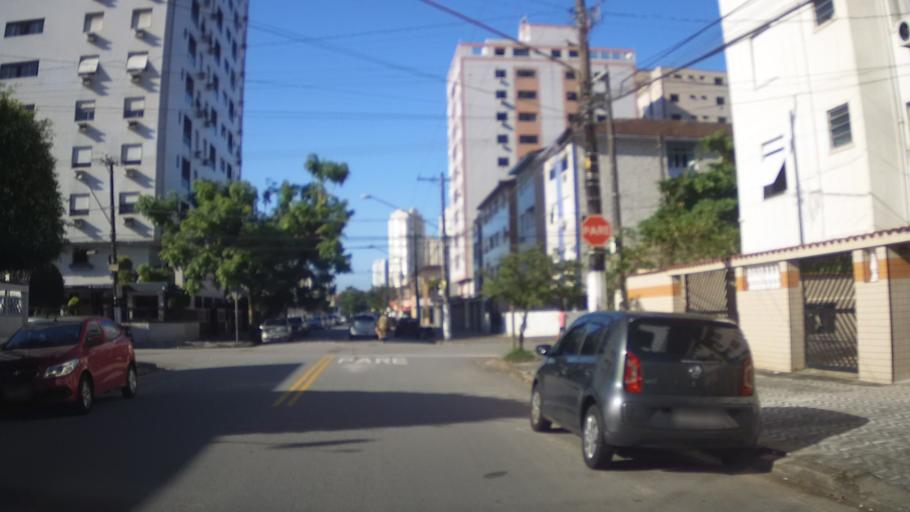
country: BR
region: Sao Paulo
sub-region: Santos
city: Santos
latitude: -23.9521
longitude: -46.3476
